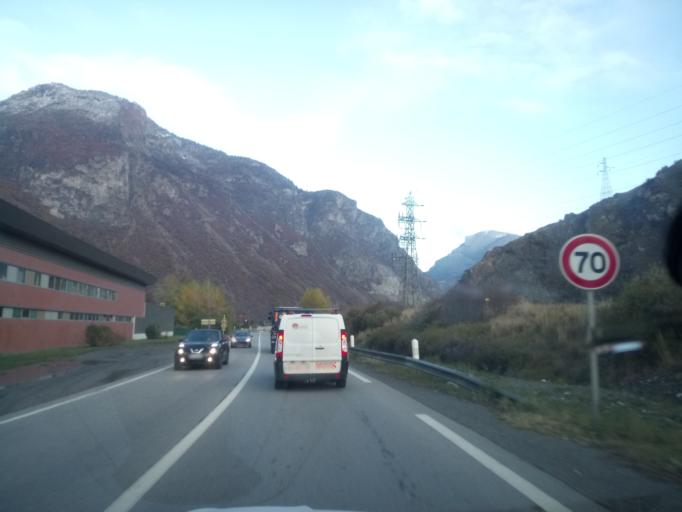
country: FR
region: Rhone-Alpes
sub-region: Departement de la Savoie
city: Saint-Jean-de-Maurienne
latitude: 45.2771
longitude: 6.3592
